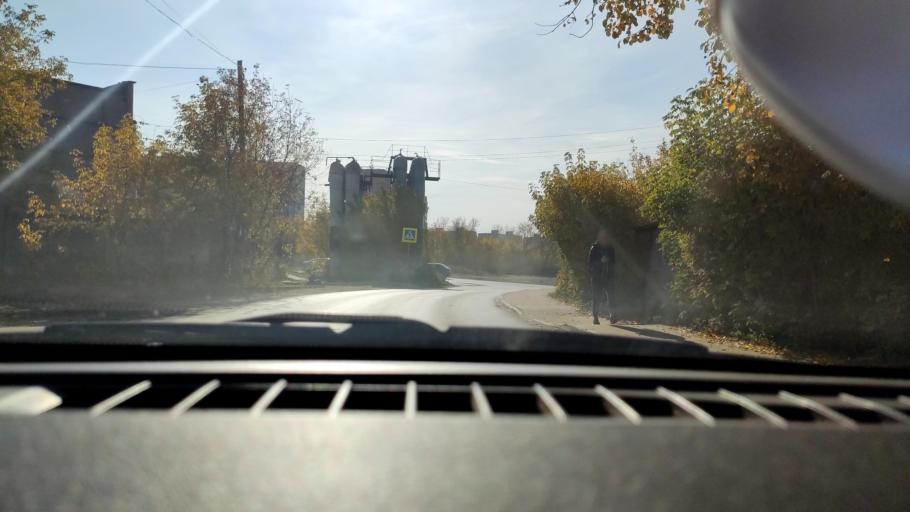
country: RU
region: Perm
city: Perm
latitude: 57.9721
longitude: 56.1929
